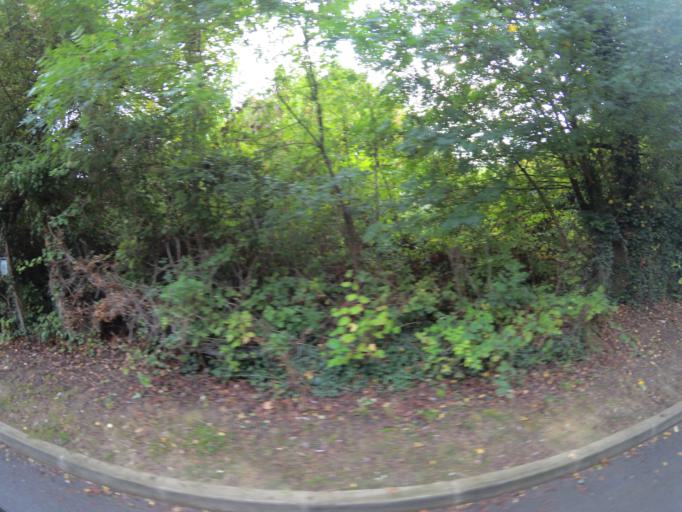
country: FR
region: Ile-de-France
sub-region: Departement de Seine-et-Marne
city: Montevrain
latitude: 48.8723
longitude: 2.7432
